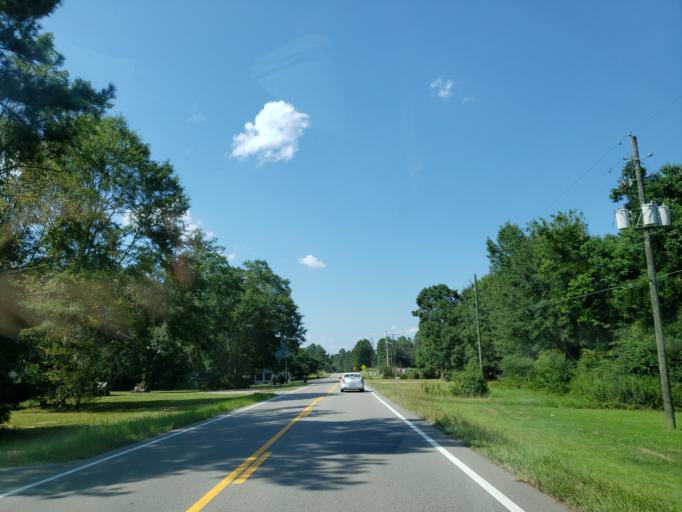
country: US
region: Mississippi
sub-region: Lamar County
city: Sumrall
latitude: 31.3965
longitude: -89.5421
